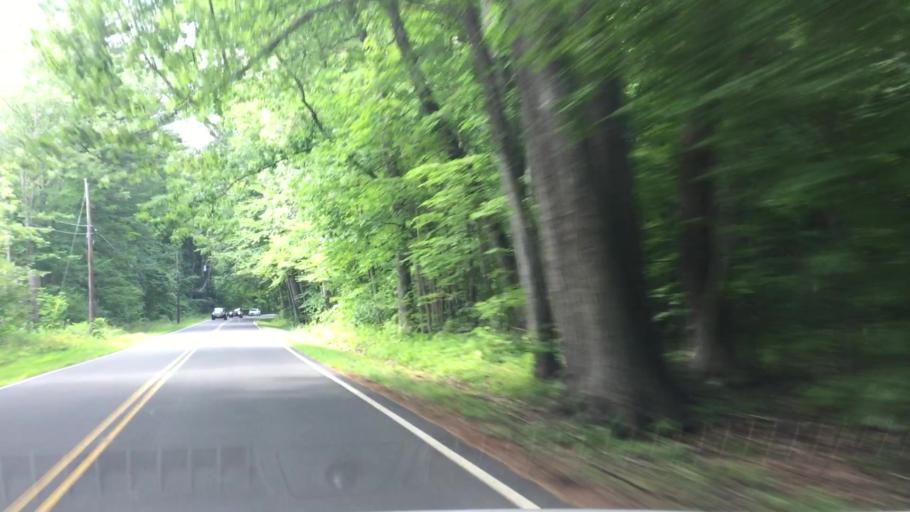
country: US
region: Massachusetts
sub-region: Berkshire County
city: Great Barrington
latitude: 42.2190
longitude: -73.4013
